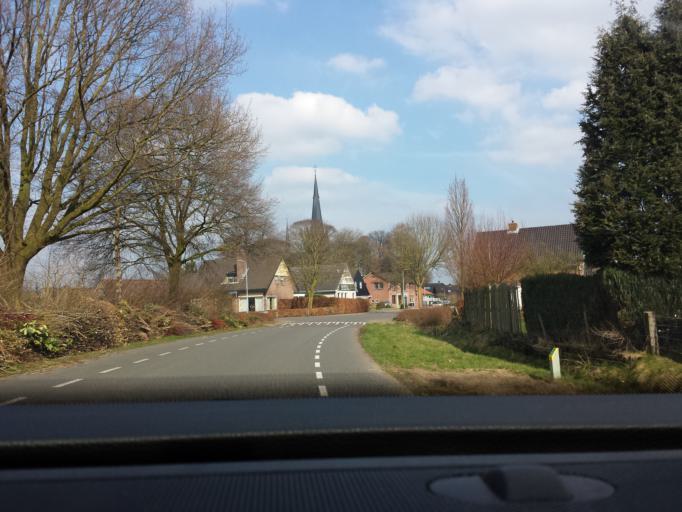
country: NL
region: Gelderland
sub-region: Oost Gelre
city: Lichtenvoorde
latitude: 52.0022
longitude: 6.5156
